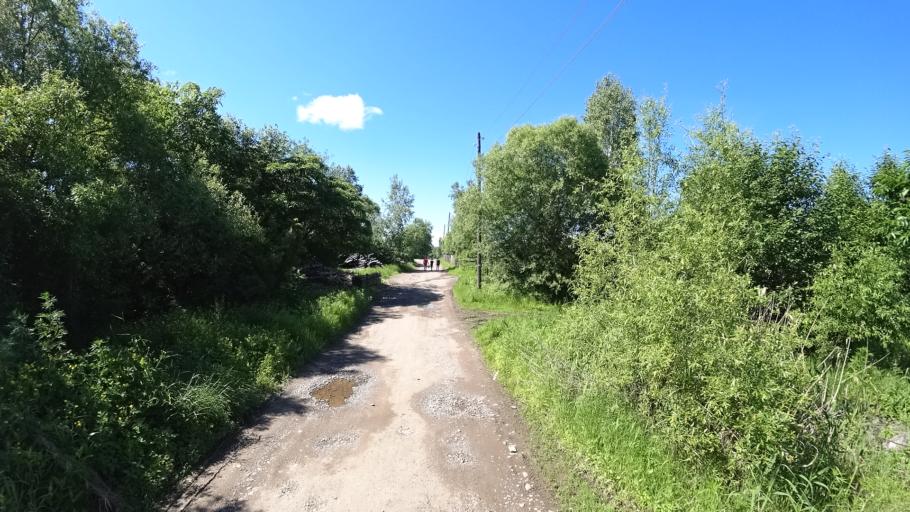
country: RU
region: Khabarovsk Krai
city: Khor
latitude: 47.8866
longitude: 135.0261
